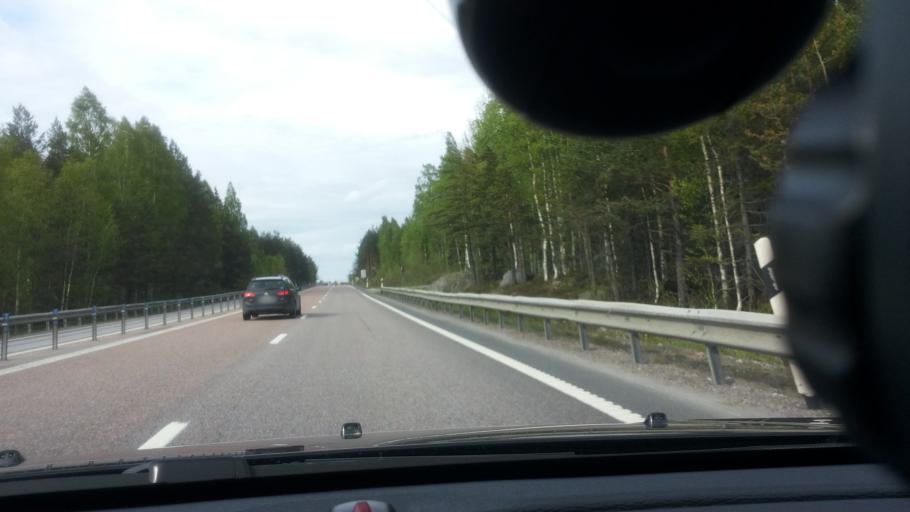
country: SE
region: Gaevleborg
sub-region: Soderhamns Kommun
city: Ljusne
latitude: 61.0883
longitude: 16.9763
